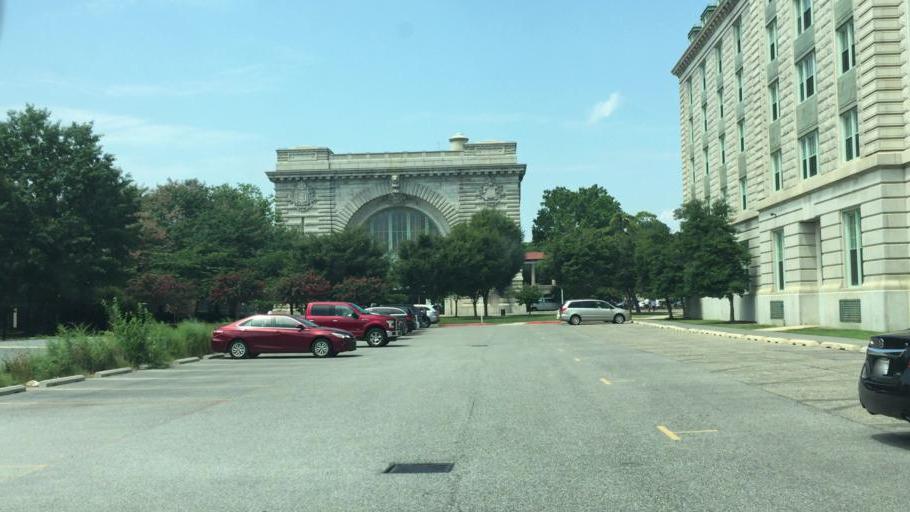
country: US
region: Maryland
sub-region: Anne Arundel County
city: Naval Academy
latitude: 38.9791
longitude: -76.4823
